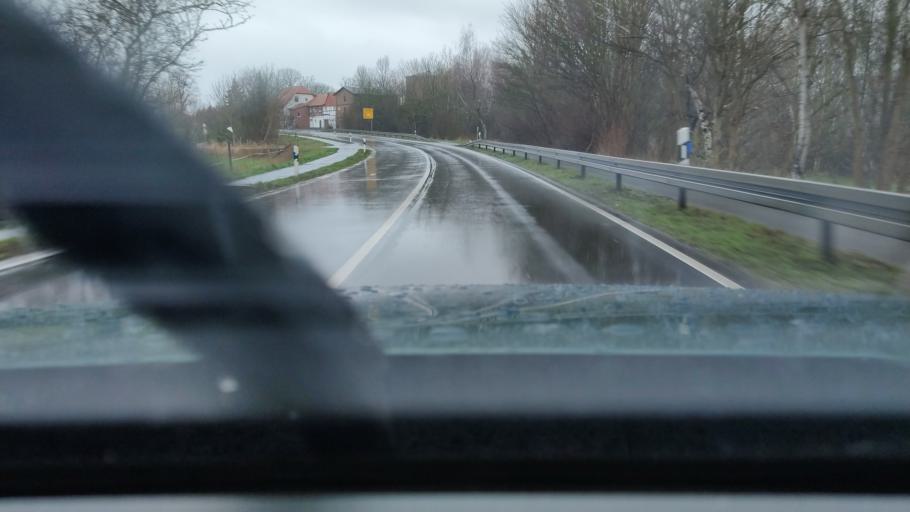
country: DE
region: Lower Saxony
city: Peine
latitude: 52.2984
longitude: 10.2323
